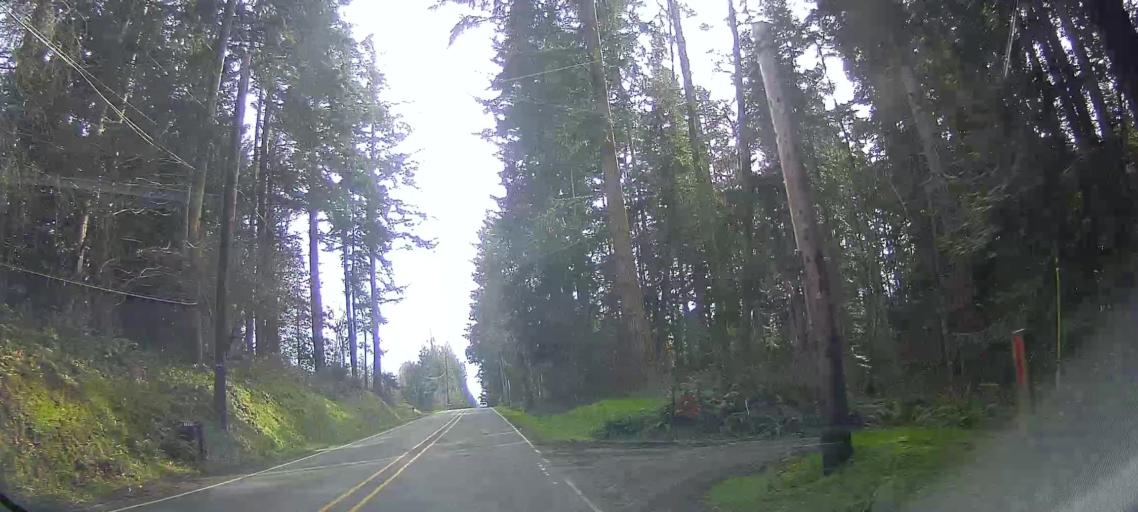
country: US
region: Washington
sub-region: Island County
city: Langley
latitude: 48.1022
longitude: -122.4177
